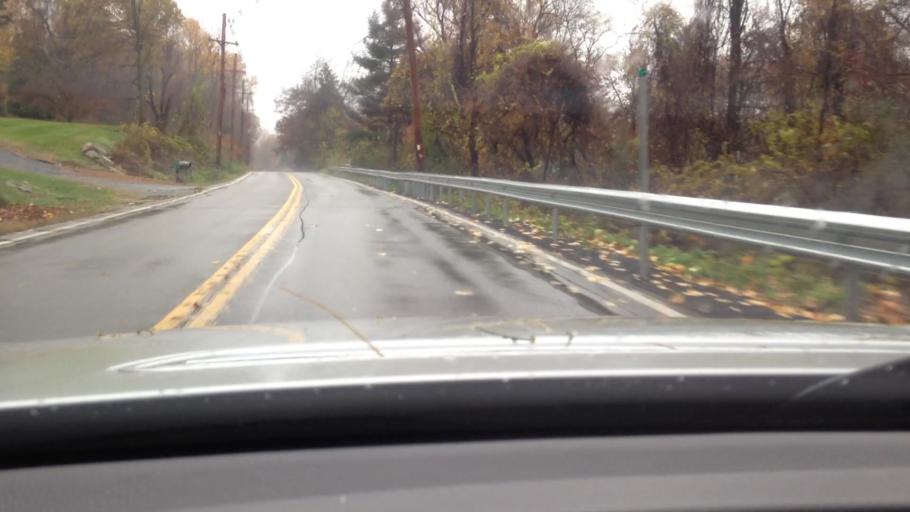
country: US
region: New York
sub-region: Orange County
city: Cornwall-on-Hudson
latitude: 41.4629
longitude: -73.9796
